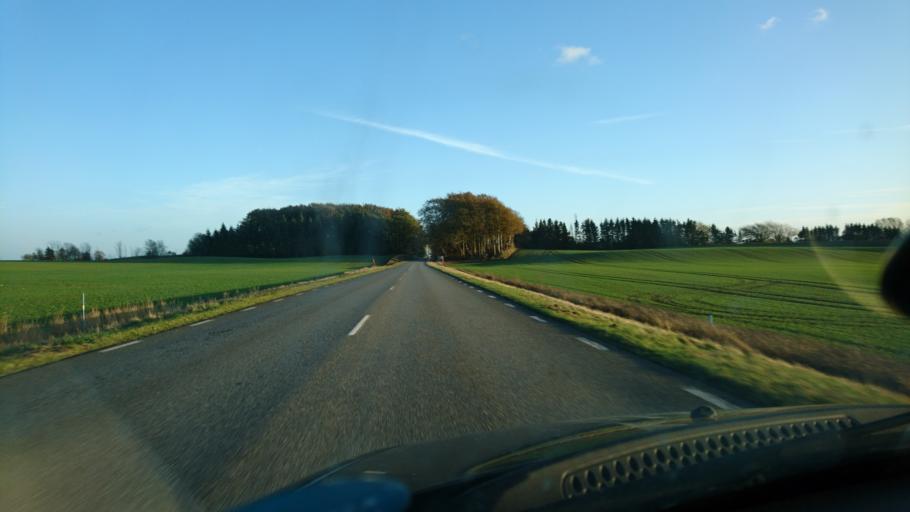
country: SE
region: Skane
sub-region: Simrishamns Kommun
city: Simrishamn
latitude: 55.4674
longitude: 14.1819
